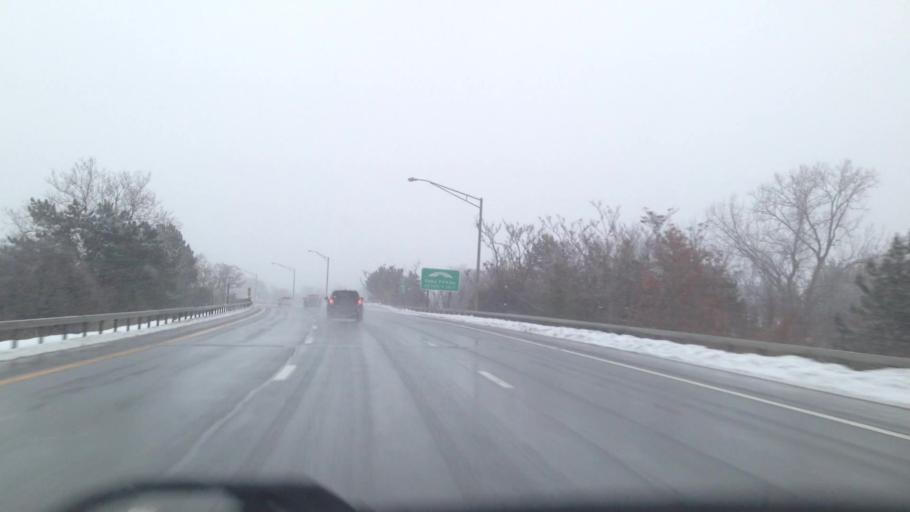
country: US
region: New York
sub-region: Onondaga County
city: Solvay
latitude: 43.0565
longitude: -76.1784
